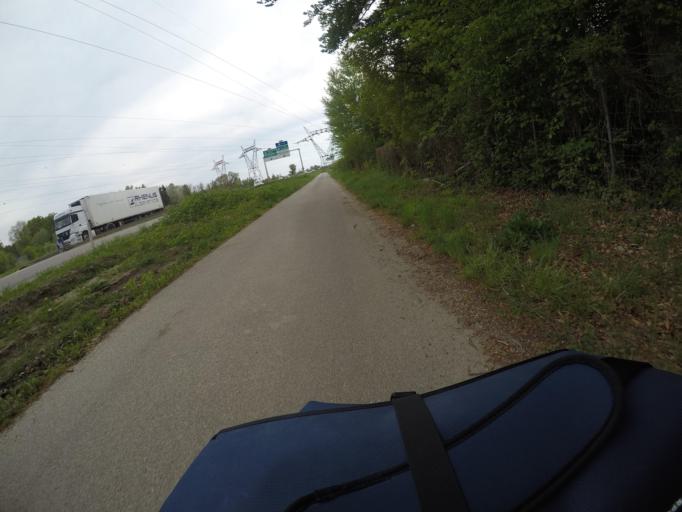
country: FR
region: Alsace
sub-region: Departement du Bas-Rhin
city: Plobsheim
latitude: 48.4976
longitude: 7.7676
